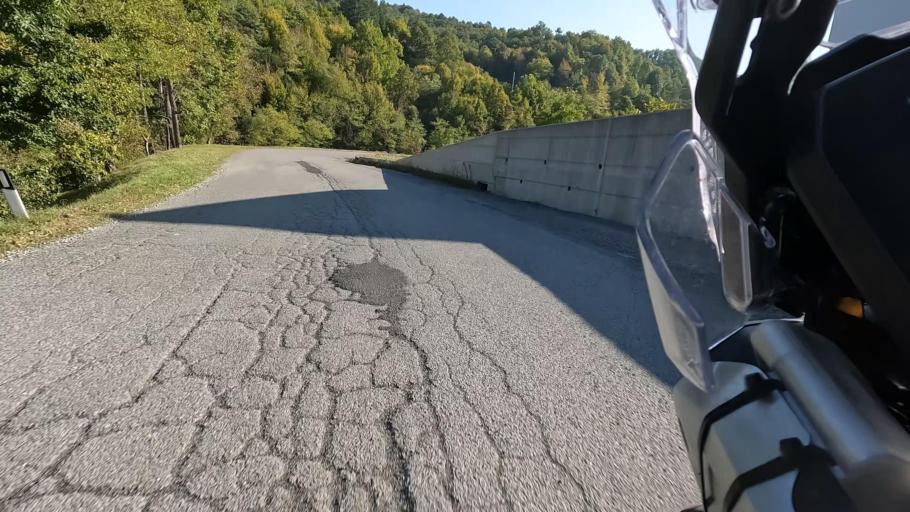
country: IT
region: Liguria
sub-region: Provincia di Savona
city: Sassello
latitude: 44.4871
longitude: 8.5048
